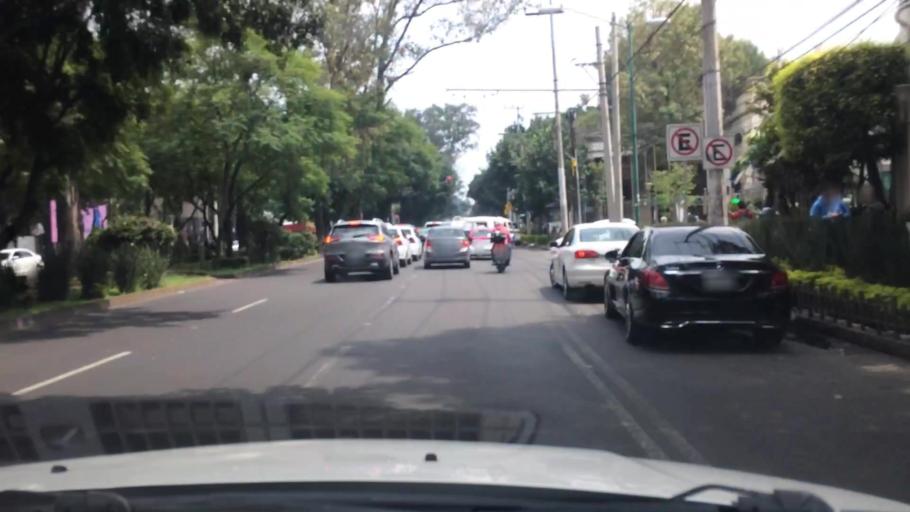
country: MX
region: Mexico City
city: Coyoacan
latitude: 19.3462
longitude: -99.1777
